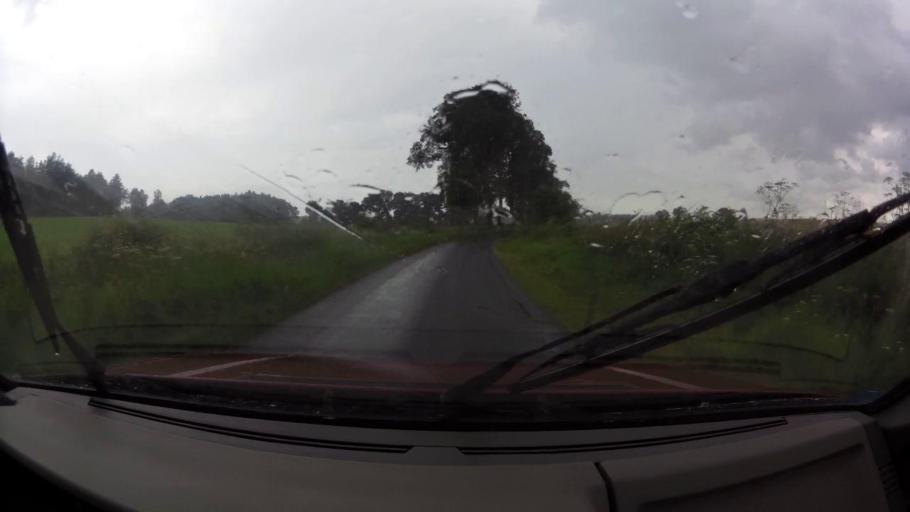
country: PL
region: West Pomeranian Voivodeship
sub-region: Koszalin
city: Koszalin
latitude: 54.0788
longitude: 16.1236
